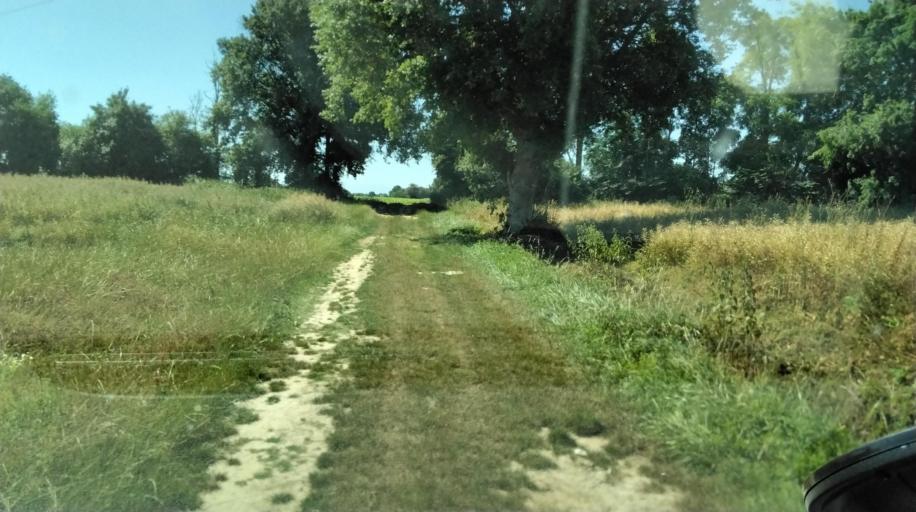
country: FR
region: Midi-Pyrenees
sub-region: Departement de la Haute-Garonne
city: Sainte-Foy-de-Peyrolieres
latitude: 43.4900
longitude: 1.1566
